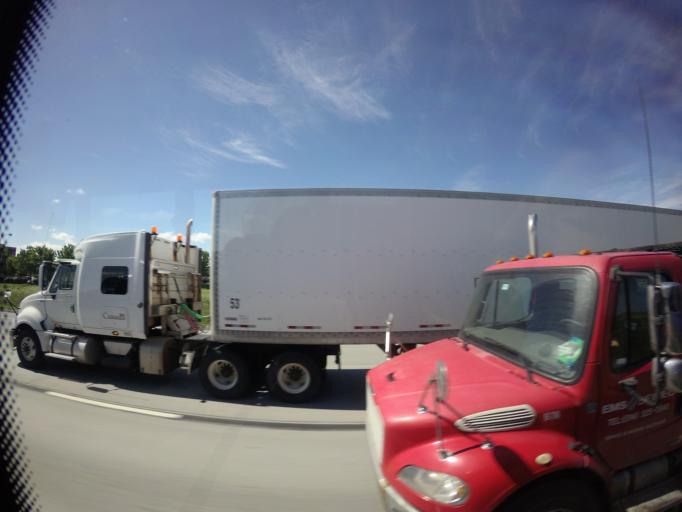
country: CA
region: Quebec
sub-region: Monteregie
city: Boucherville
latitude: 45.5722
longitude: -73.4469
